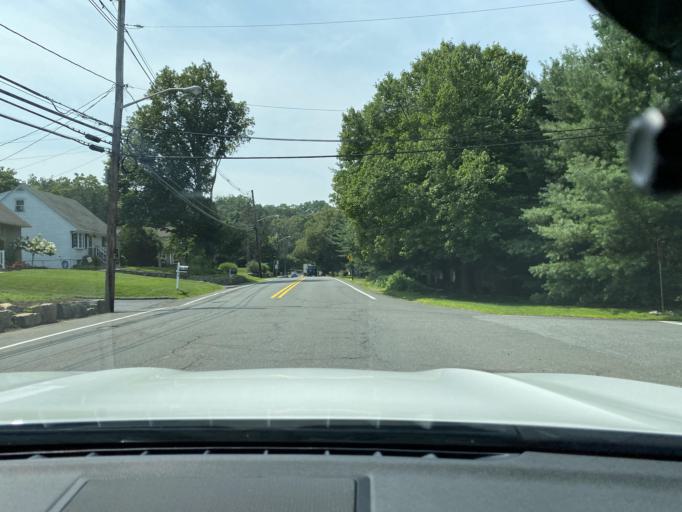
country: US
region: New Jersey
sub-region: Bergen County
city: Franklin Lakes
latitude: 41.0432
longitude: -74.2267
